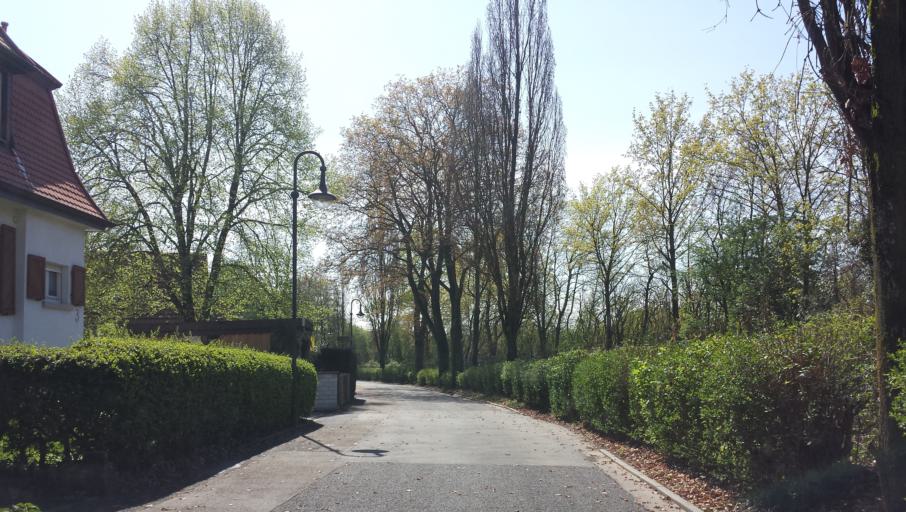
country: DE
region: Hesse
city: Sulzbach
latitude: 50.1035
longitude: 8.5293
